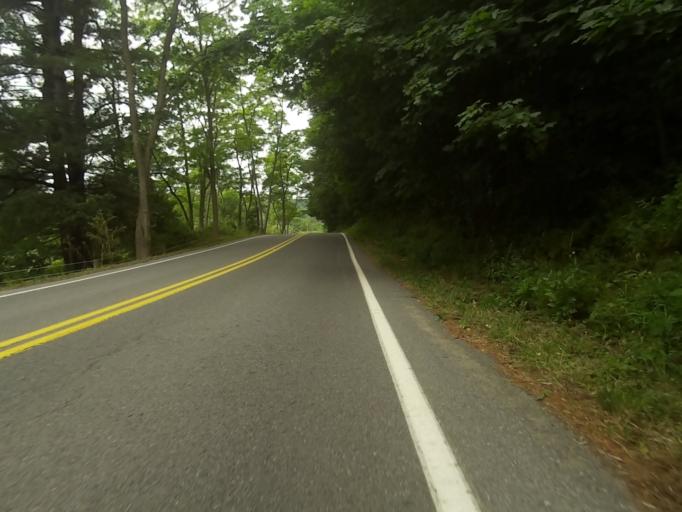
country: US
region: Pennsylvania
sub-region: Centre County
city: Stormstown
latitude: 40.7213
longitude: -78.0208
